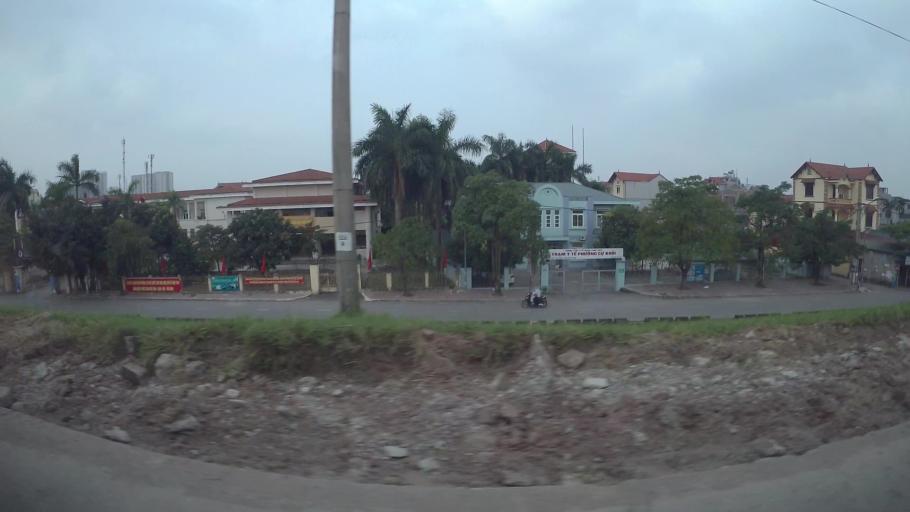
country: VN
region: Ha Noi
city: Trau Quy
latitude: 21.0110
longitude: 105.9048
